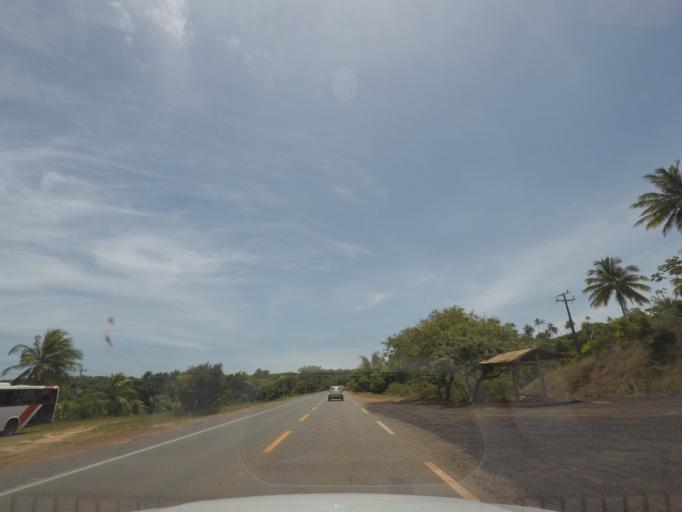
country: BR
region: Bahia
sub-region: Mata De Sao Joao
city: Mata de Sao Joao
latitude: -12.4299
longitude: -37.9406
